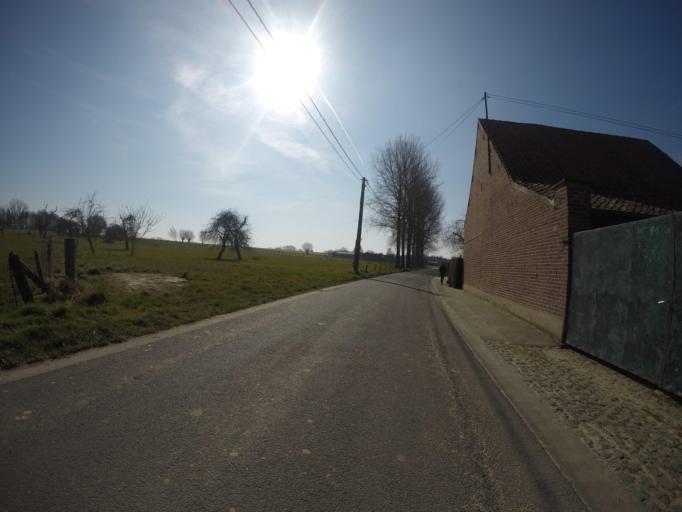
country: BE
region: Flanders
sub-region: Provincie Oost-Vlaanderen
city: Sint-Maria-Lierde
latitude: 50.7960
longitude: 3.8412
